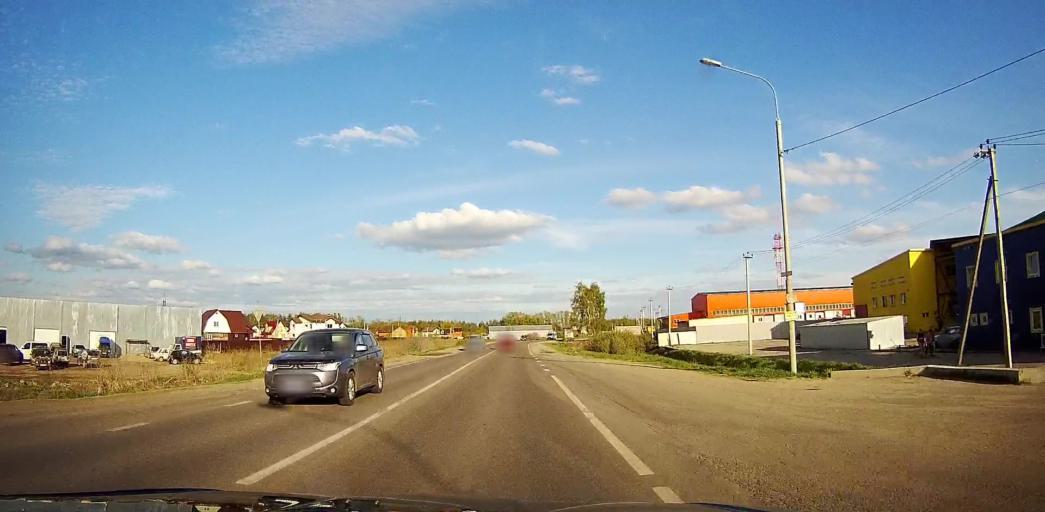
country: RU
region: Moskovskaya
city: Malyshevo
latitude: 55.4839
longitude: 38.3398
